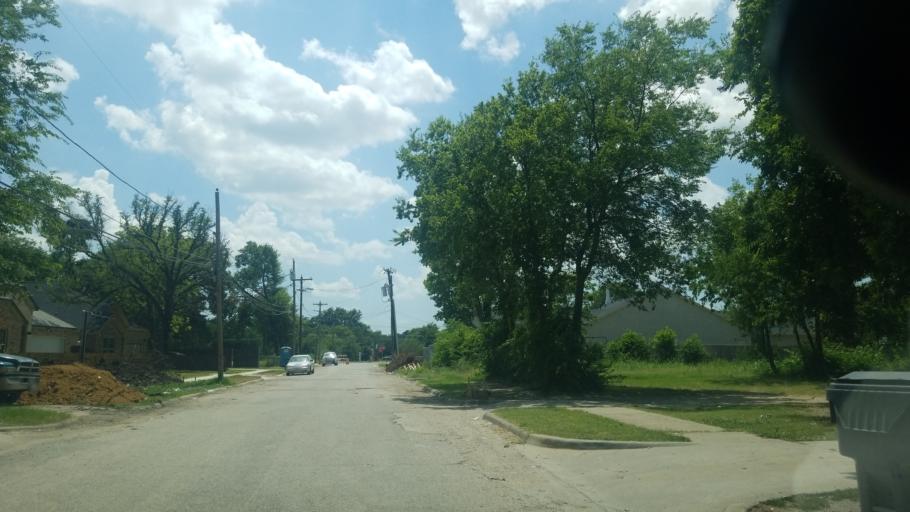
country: US
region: Texas
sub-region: Dallas County
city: Dallas
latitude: 32.7148
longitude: -96.7745
